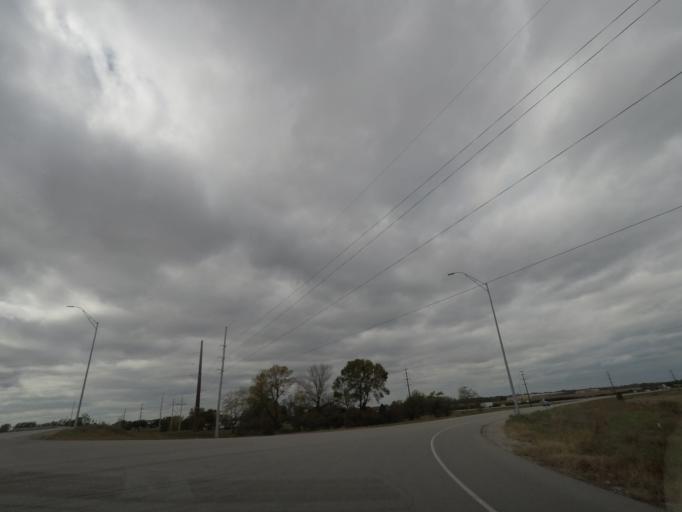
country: US
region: Iowa
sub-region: Story County
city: Huxley
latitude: 41.8779
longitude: -93.5688
